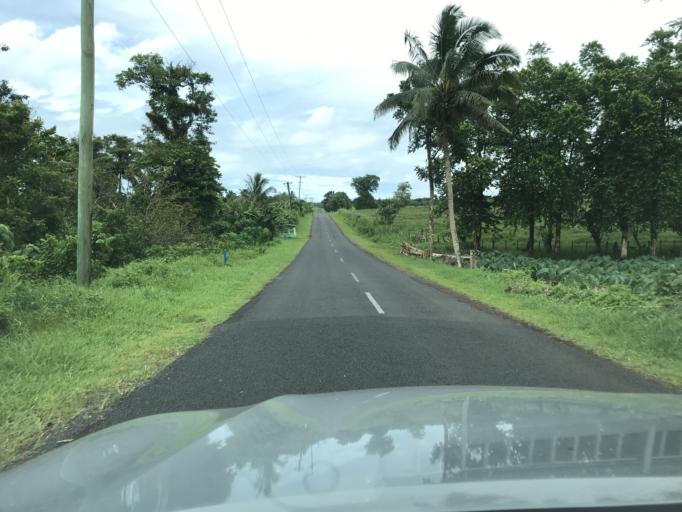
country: WS
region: A'ana
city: Leulumoega
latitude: -13.8773
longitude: -171.9374
